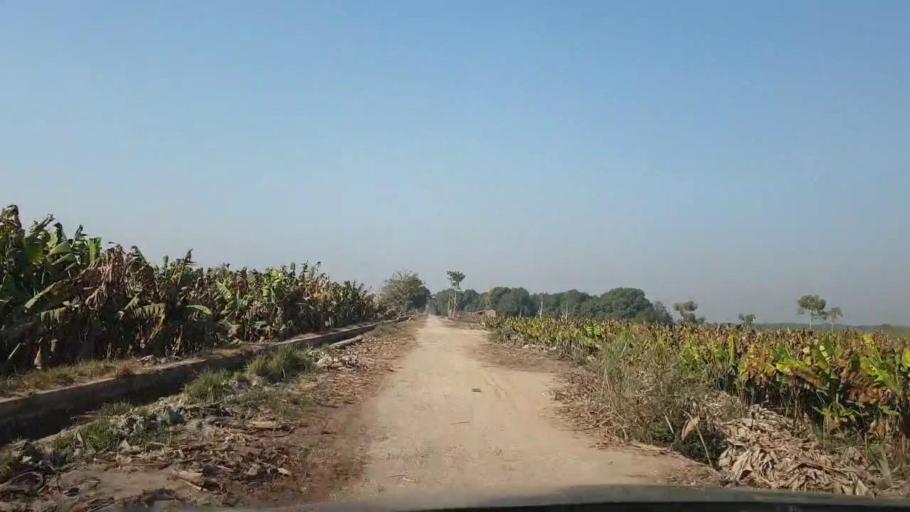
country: PK
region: Sindh
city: Tando Allahyar
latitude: 25.5152
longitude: 68.7037
